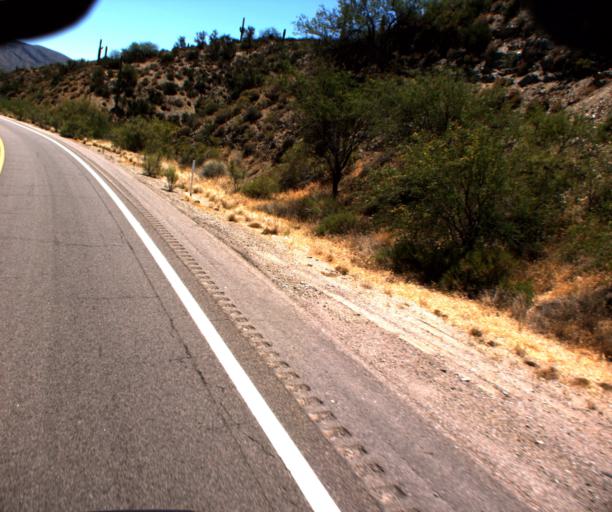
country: US
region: Arizona
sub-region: Pinal County
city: Superior
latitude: 33.1748
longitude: -111.0258
